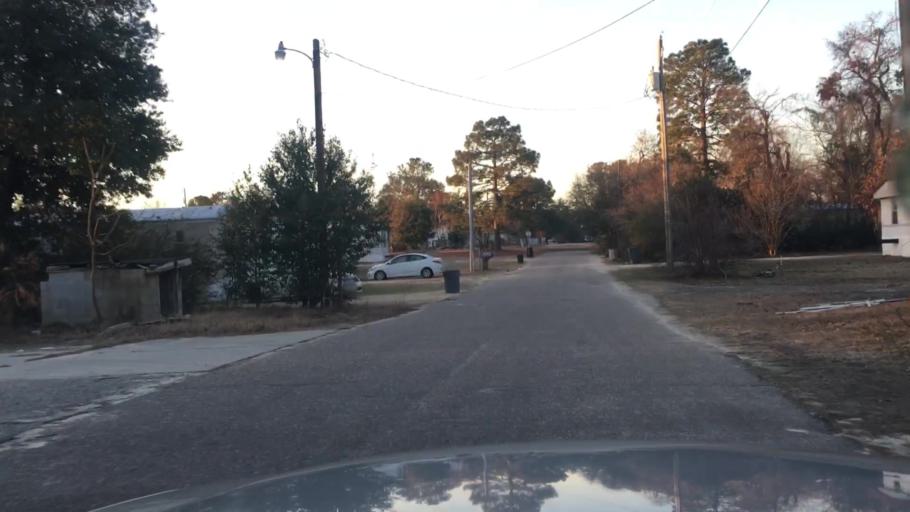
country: US
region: North Carolina
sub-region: Cumberland County
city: Hope Mills
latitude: 34.9842
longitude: -78.9084
